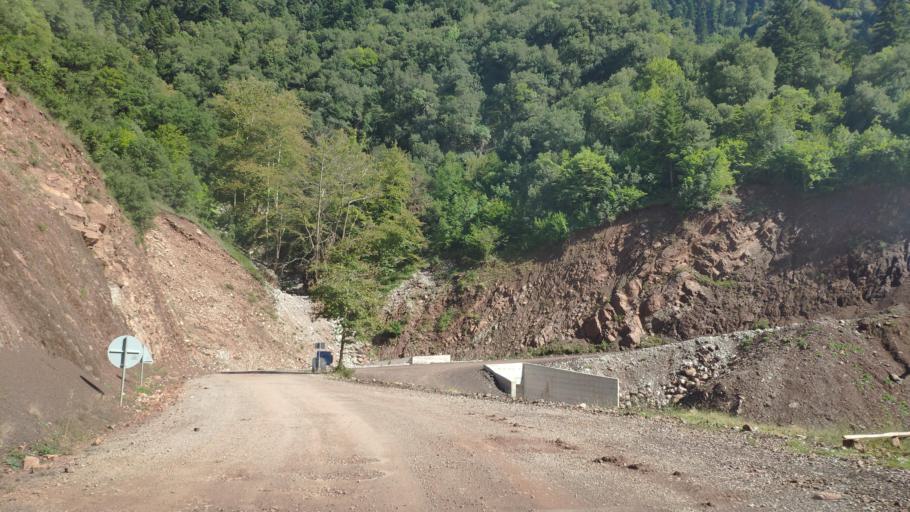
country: GR
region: Central Greece
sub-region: Nomos Evrytanias
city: Kerasochori
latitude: 39.1266
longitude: 21.6274
